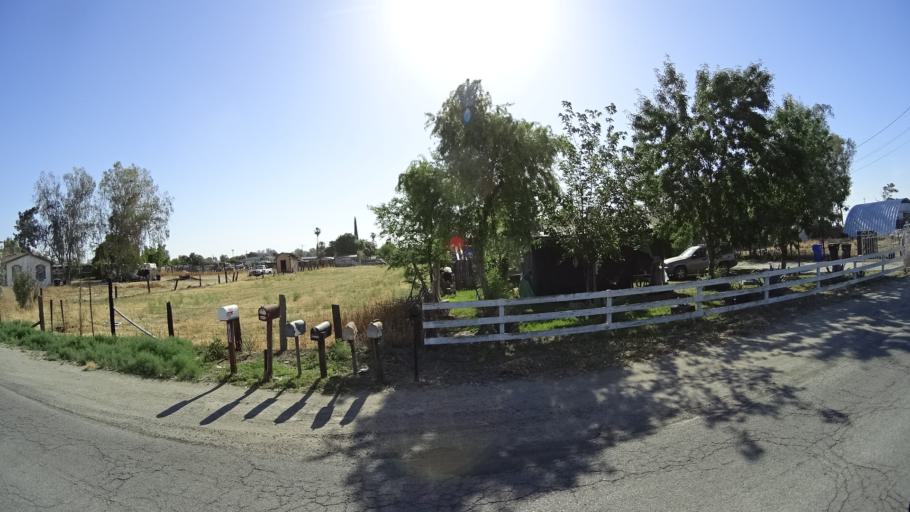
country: US
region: California
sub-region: Kings County
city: Corcoran
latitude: 36.0956
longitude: -119.5899
